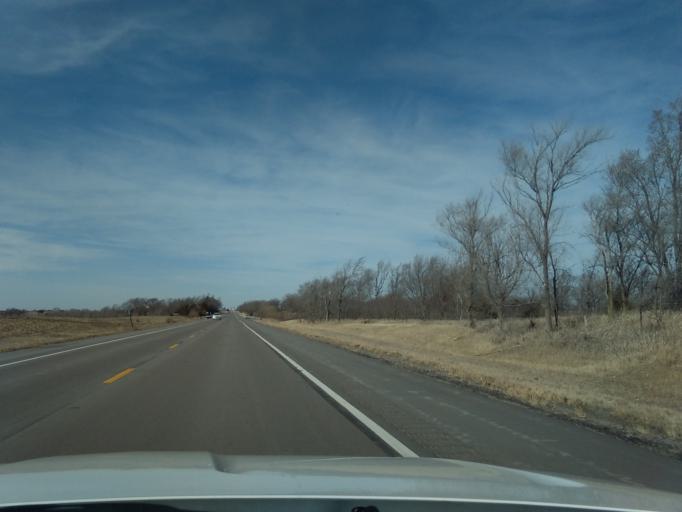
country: US
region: Nebraska
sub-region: Saline County
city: Friend
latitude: 40.6506
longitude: -97.3564
